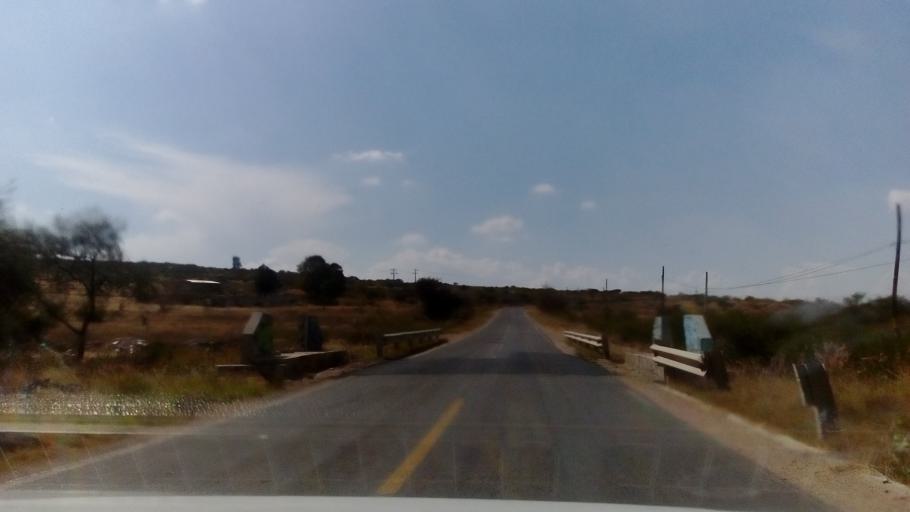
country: MX
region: Guanajuato
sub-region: Silao de la Victoria
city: San Francisco (Banos de Agua Caliente)
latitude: 21.0749
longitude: -101.4840
